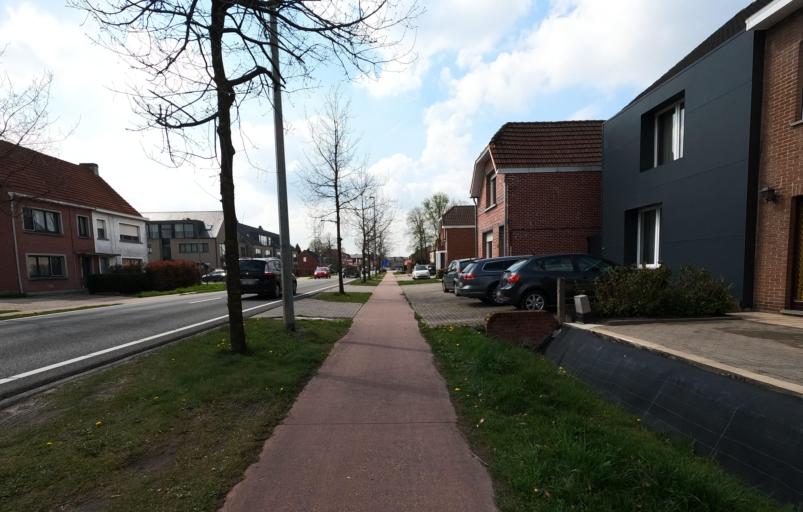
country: BE
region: Flanders
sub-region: Provincie Antwerpen
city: Schilde
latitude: 51.3062
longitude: 4.5713
